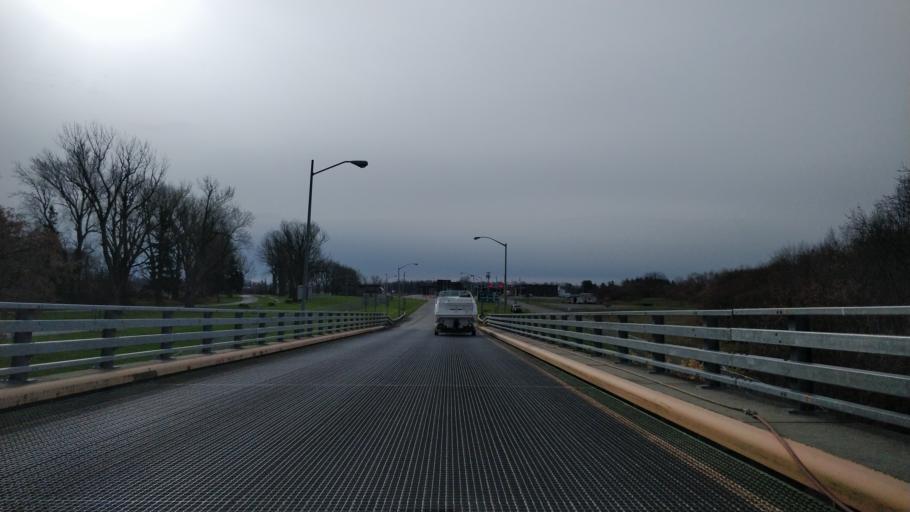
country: US
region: New York
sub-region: St. Lawrence County
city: Ogdensburg
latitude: 44.7265
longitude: -75.4552
